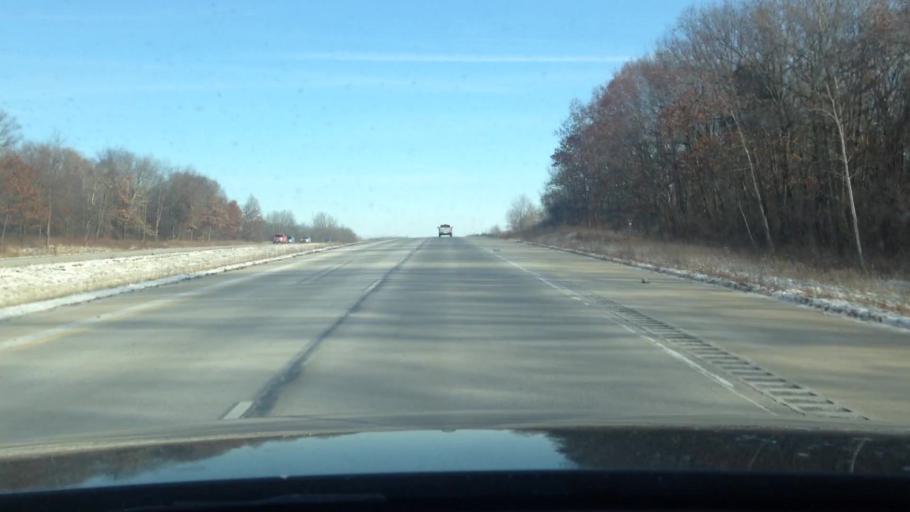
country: US
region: Wisconsin
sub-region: Walworth County
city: Potter Lake
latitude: 42.8300
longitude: -88.3502
